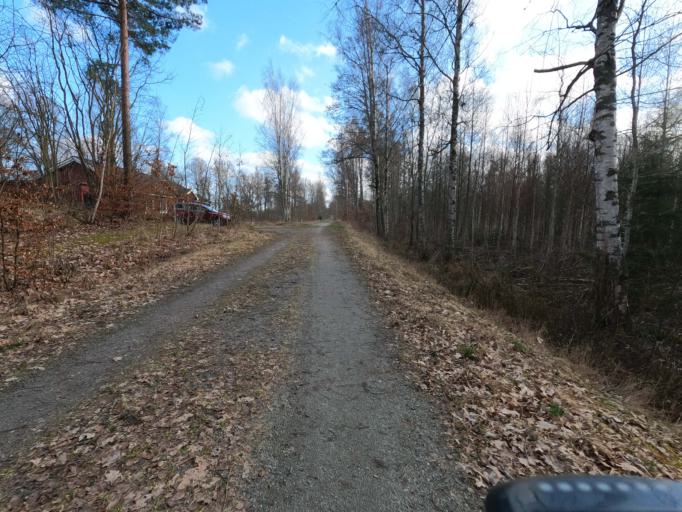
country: SE
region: Kronoberg
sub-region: Vaxjo Kommun
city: Gemla
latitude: 56.6876
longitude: 14.6078
